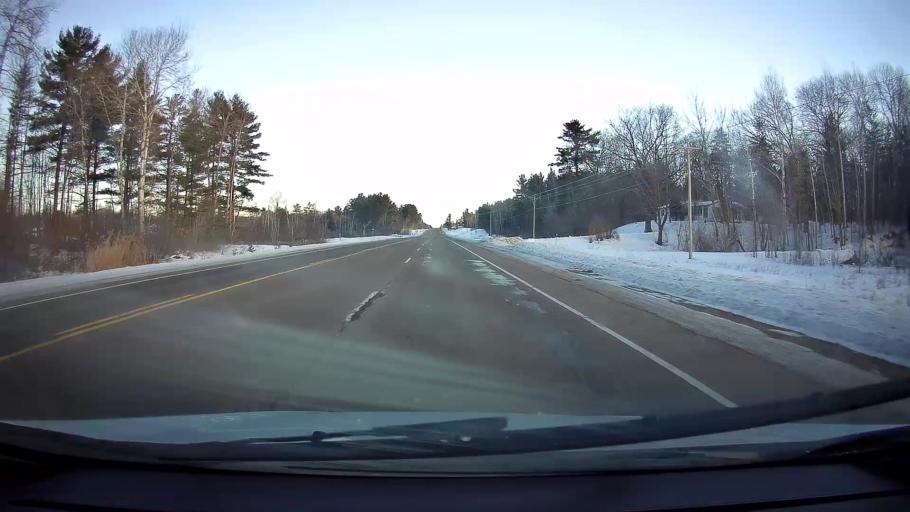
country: US
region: Wisconsin
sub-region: Barron County
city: Cumberland
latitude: 45.5659
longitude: -92.0173
